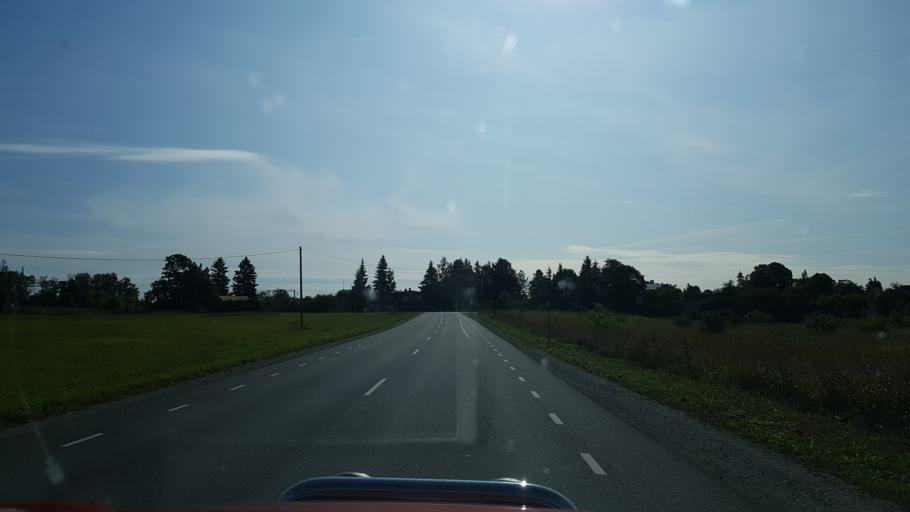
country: EE
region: Harju
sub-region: Joelaehtme vald
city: Loo
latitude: 59.3978
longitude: 24.9299
